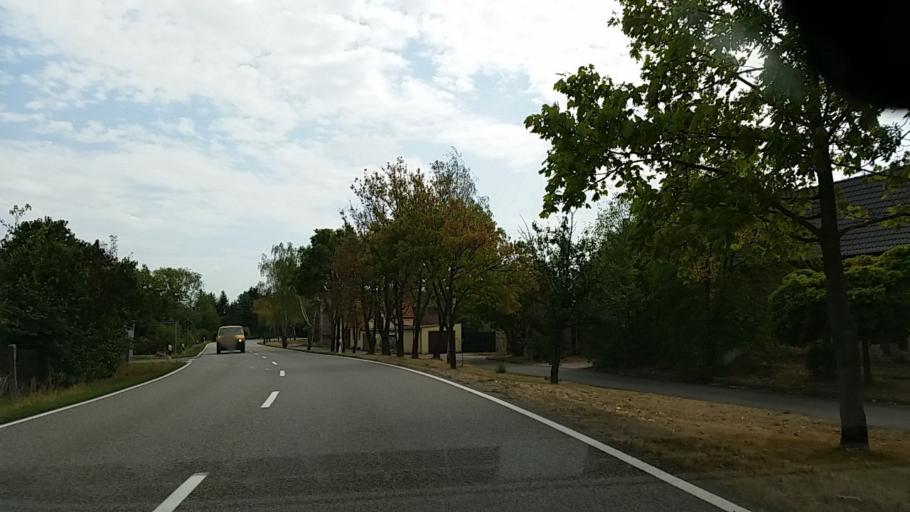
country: DE
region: Saxony-Anhalt
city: Steigra
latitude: 51.3022
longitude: 11.6585
